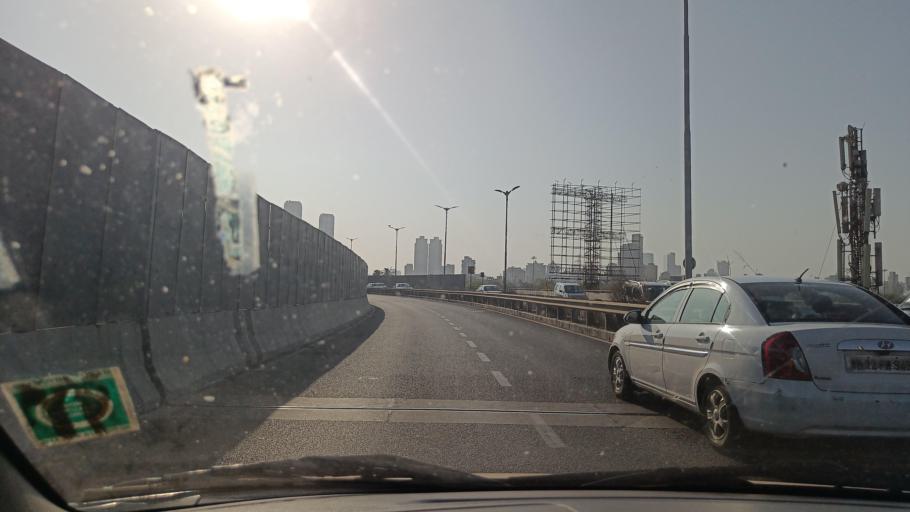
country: IN
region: Maharashtra
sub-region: Mumbai Suburban
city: Mumbai
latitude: 19.0107
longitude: 72.8672
